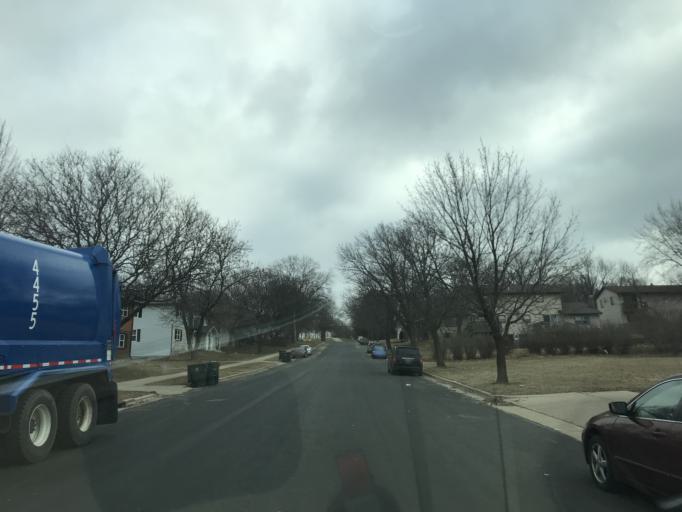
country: US
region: Wisconsin
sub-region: Dane County
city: Monona
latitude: 43.1102
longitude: -89.3085
